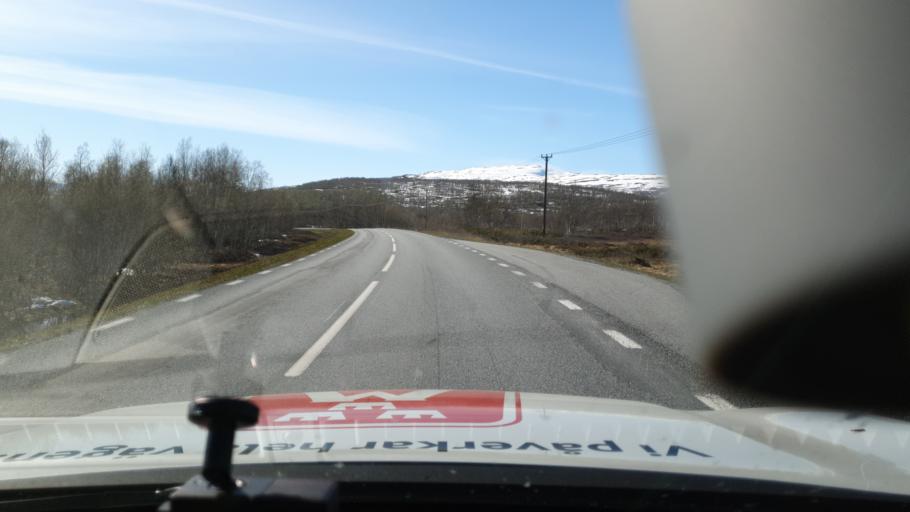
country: NO
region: Nordland
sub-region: Rana
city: Mo i Rana
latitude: 66.0366
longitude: 15.0647
